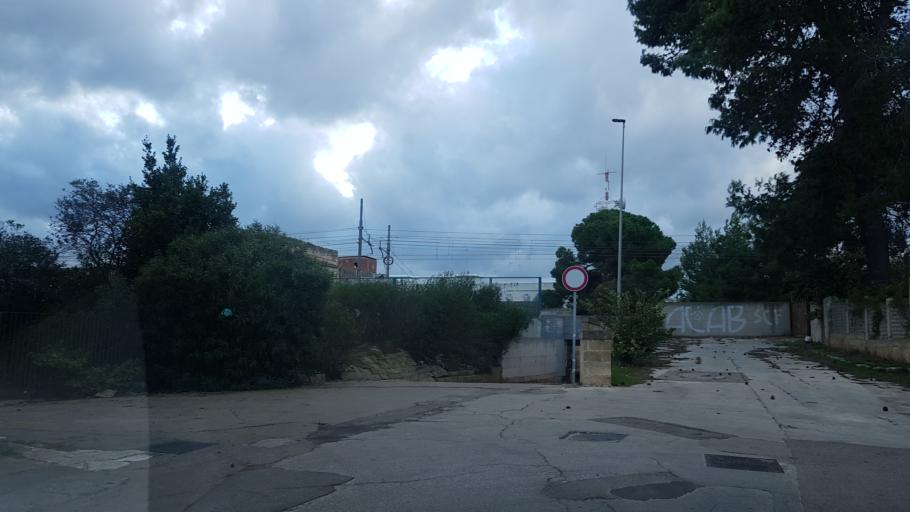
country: IT
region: Apulia
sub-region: Provincia di Brindisi
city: San Pietro Vernotico
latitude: 40.4879
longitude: 18.0018
